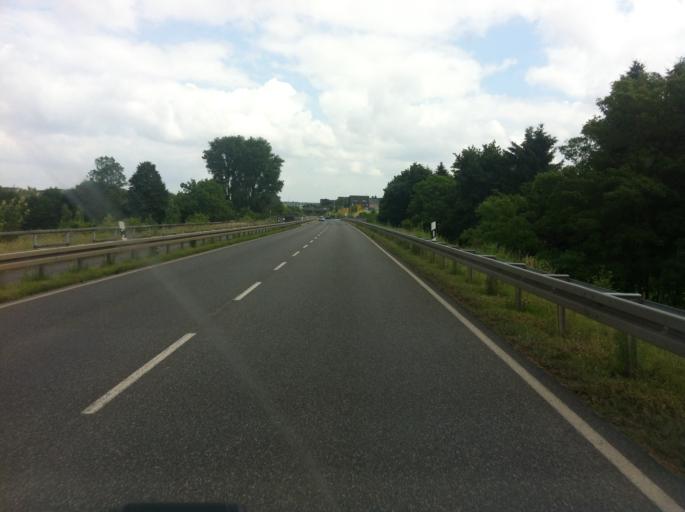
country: DE
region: North Rhine-Westphalia
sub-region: Regierungsbezirk Koln
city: Weilerswist
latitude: 50.7485
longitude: 6.8300
